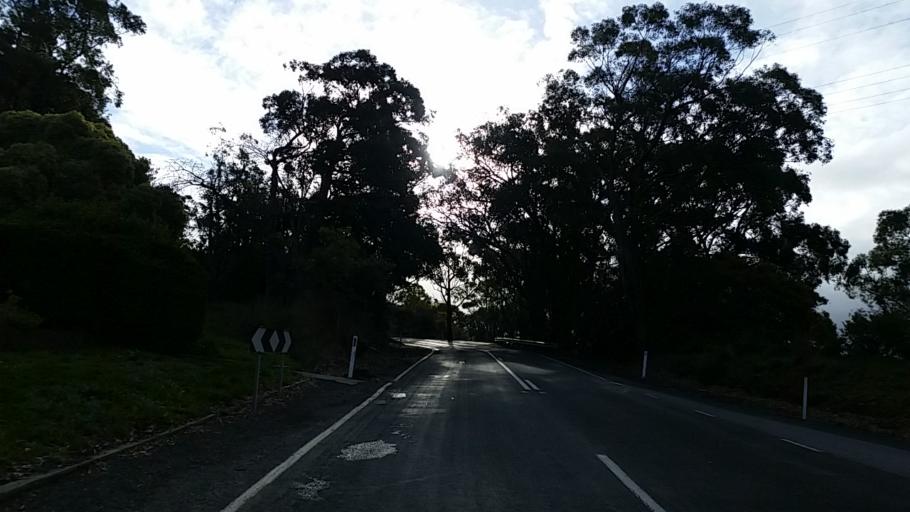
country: AU
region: South Australia
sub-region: Adelaide Hills
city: Bridgewater
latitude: -34.9641
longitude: 138.7669
